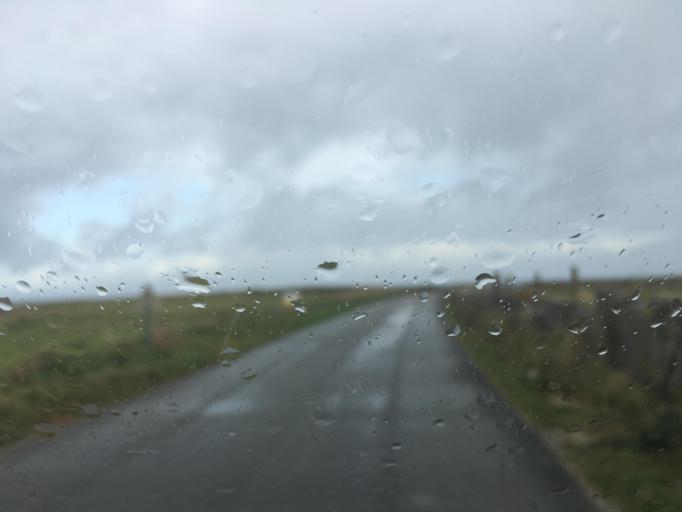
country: FR
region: Lower Normandy
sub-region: Departement de la Manche
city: Reville
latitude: 49.6932
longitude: -1.2772
